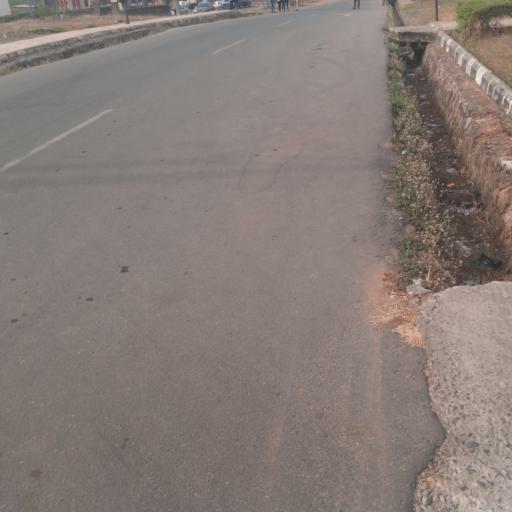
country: NG
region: Ondo
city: Ilare
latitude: 7.2980
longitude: 5.1356
